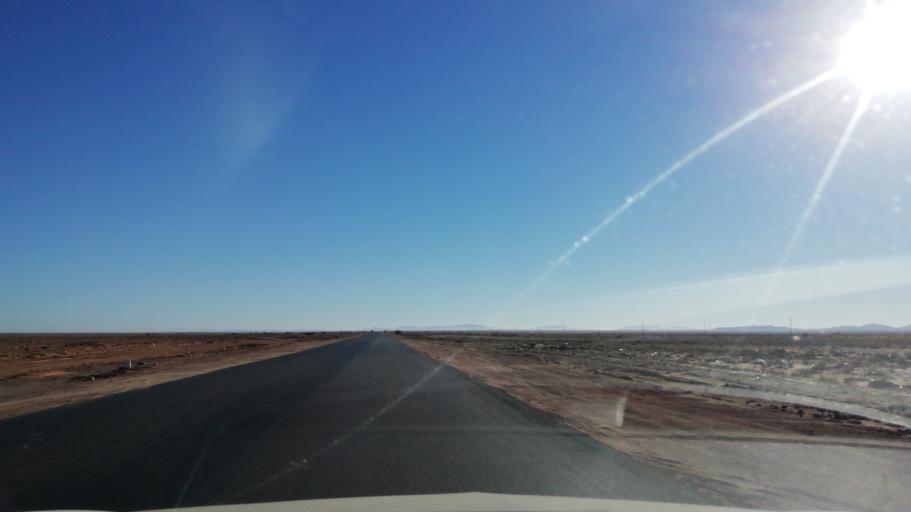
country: DZ
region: El Bayadh
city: El Bayadh
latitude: 33.8578
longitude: 0.5777
